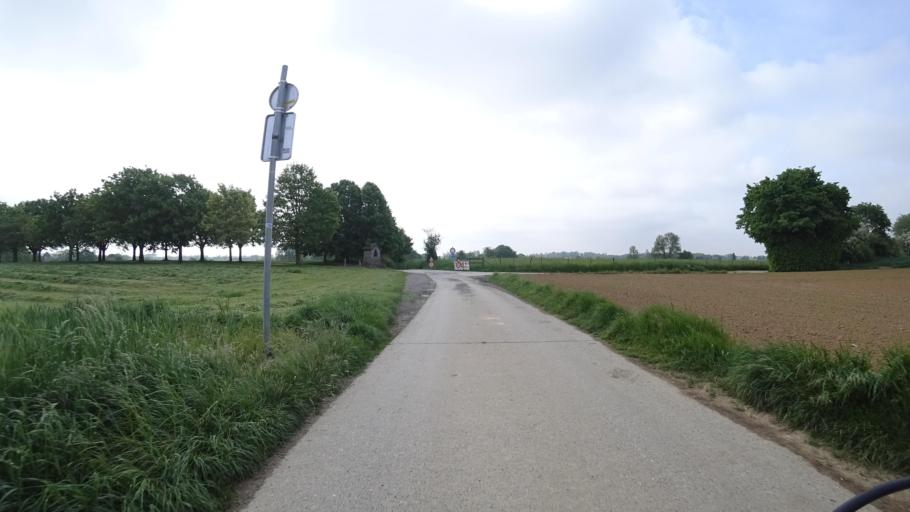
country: BE
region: Wallonia
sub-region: Province du Brabant Wallon
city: Louvain-la-Neuve
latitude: 50.6693
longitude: 4.6674
